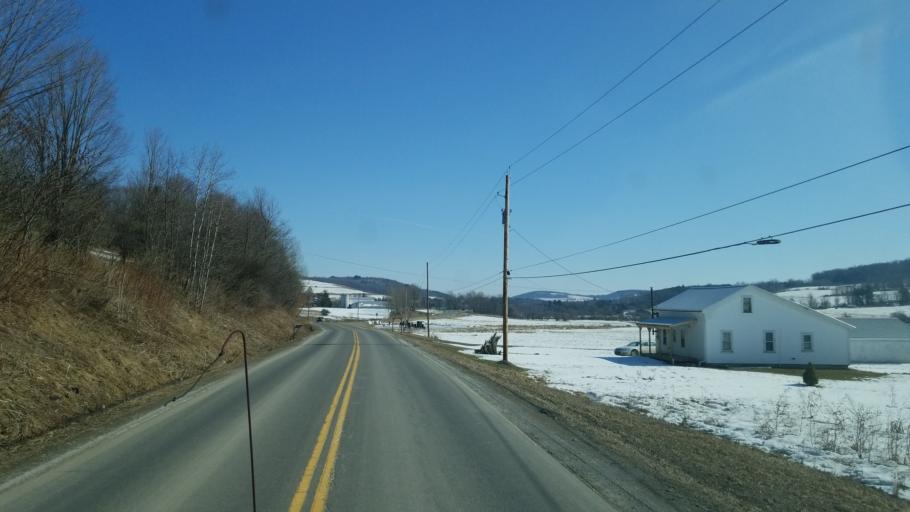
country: US
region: Pennsylvania
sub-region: Tioga County
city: Elkland
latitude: 42.0759
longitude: -77.4255
